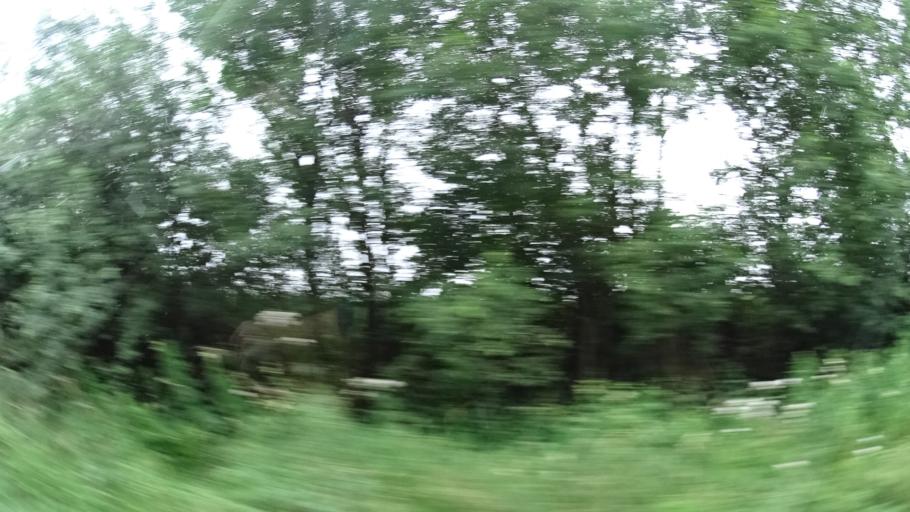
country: BE
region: Wallonia
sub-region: Province du Luxembourg
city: Habay-la-Vieille
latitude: 49.7115
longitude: 5.6977
